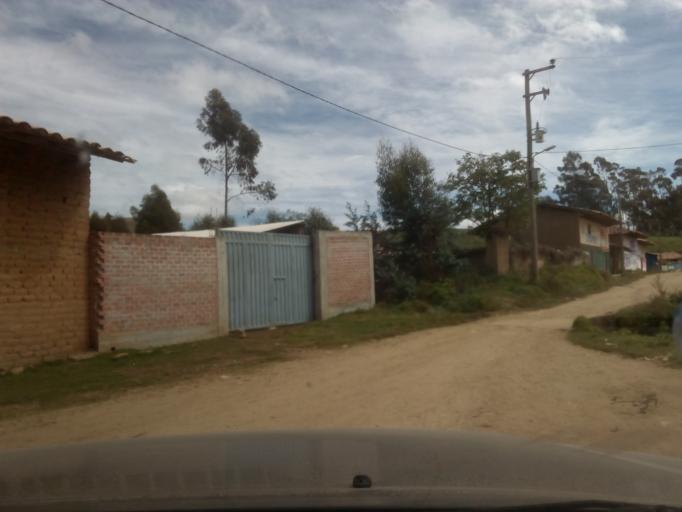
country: PE
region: La Libertad
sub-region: Sanchez Carrion
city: Curgos
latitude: -7.8572
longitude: -77.9769
